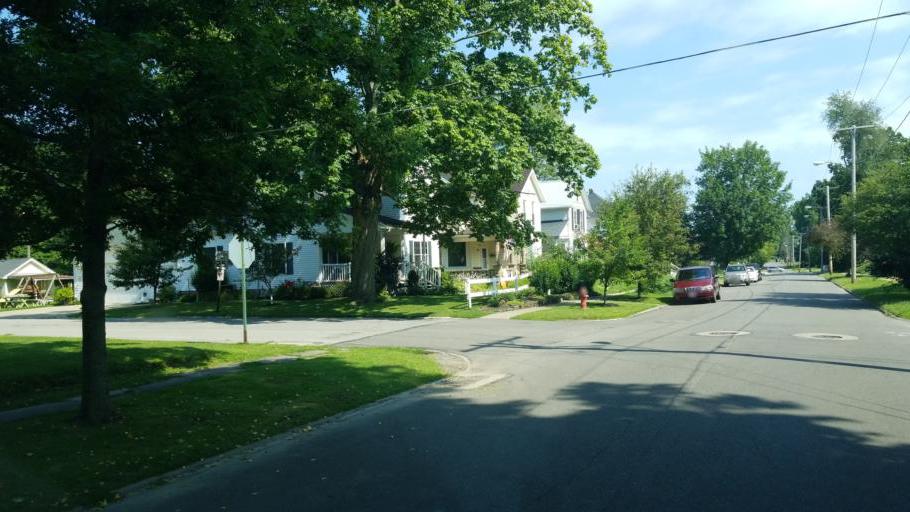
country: US
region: Ohio
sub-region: Crawford County
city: Galion
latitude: 40.7363
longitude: -82.7945
